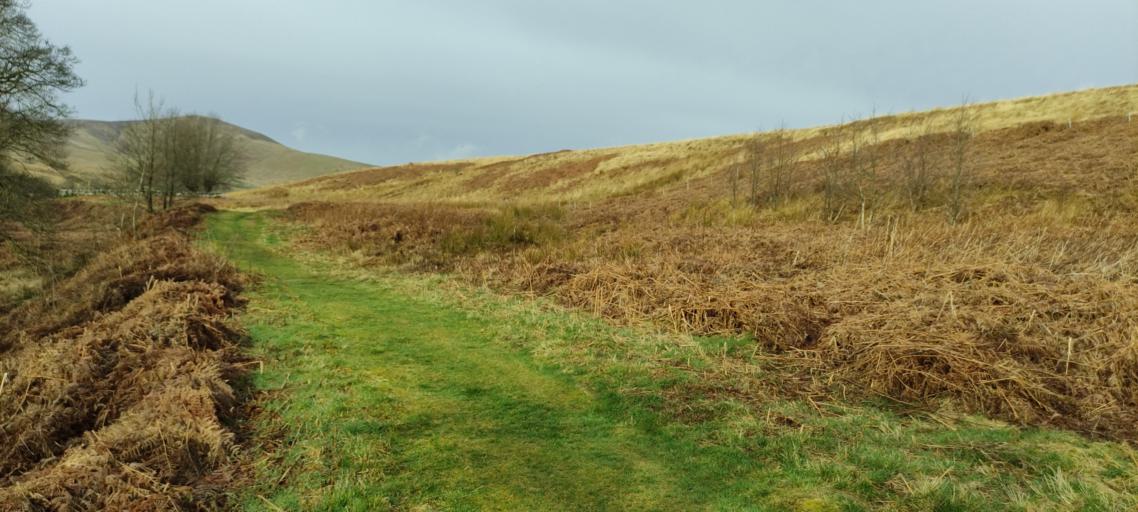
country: GB
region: Scotland
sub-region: The Scottish Borders
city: Hawick
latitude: 55.2555
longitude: -2.7961
